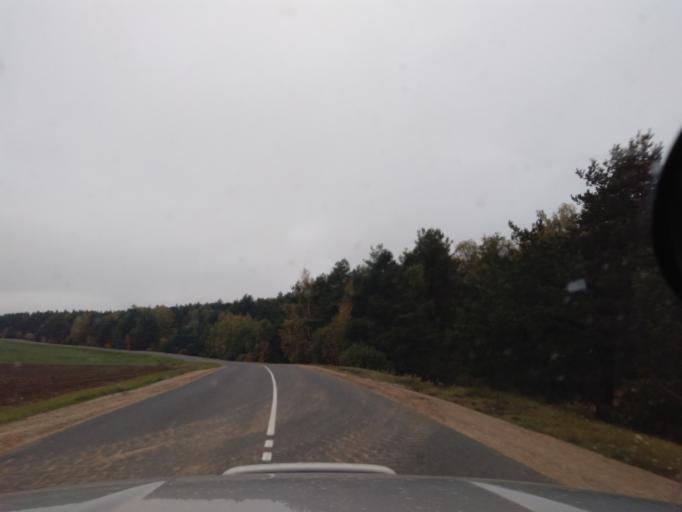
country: BY
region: Minsk
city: Kapyl'
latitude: 53.1555
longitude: 27.2272
